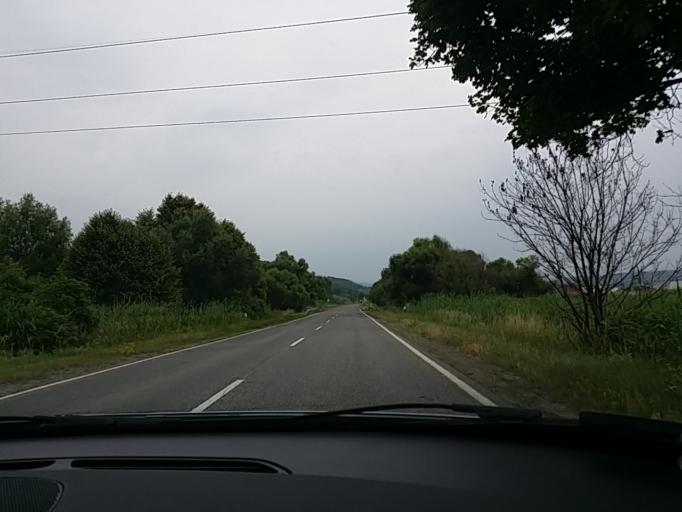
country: HU
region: Nograd
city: Batonyterenye
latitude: 47.9884
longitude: 19.8150
